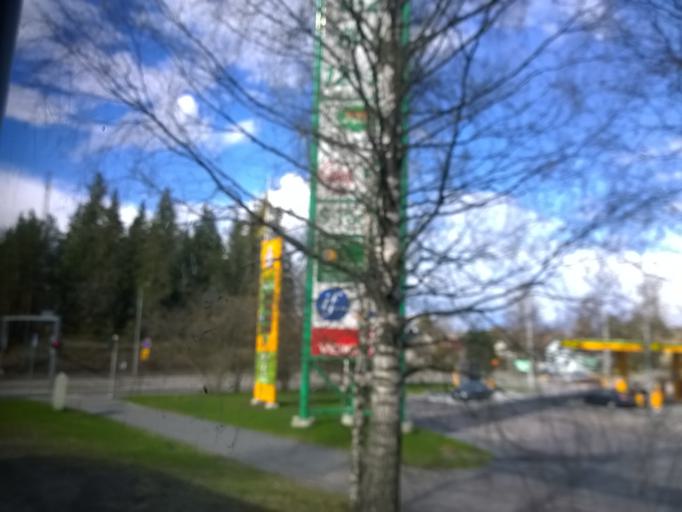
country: FI
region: Pirkanmaa
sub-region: Tampere
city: Tampere
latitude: 61.4691
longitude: 23.7751
